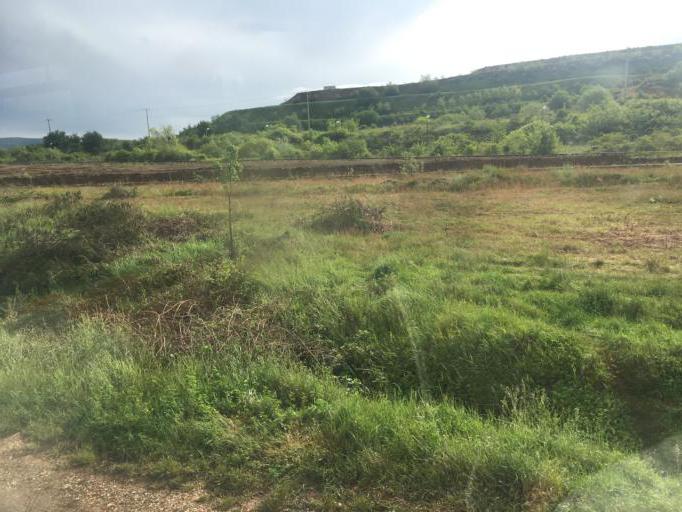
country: XK
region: Pristina
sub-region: Komuna e Drenasit
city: Glogovac
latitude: 42.6390
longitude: 20.9075
